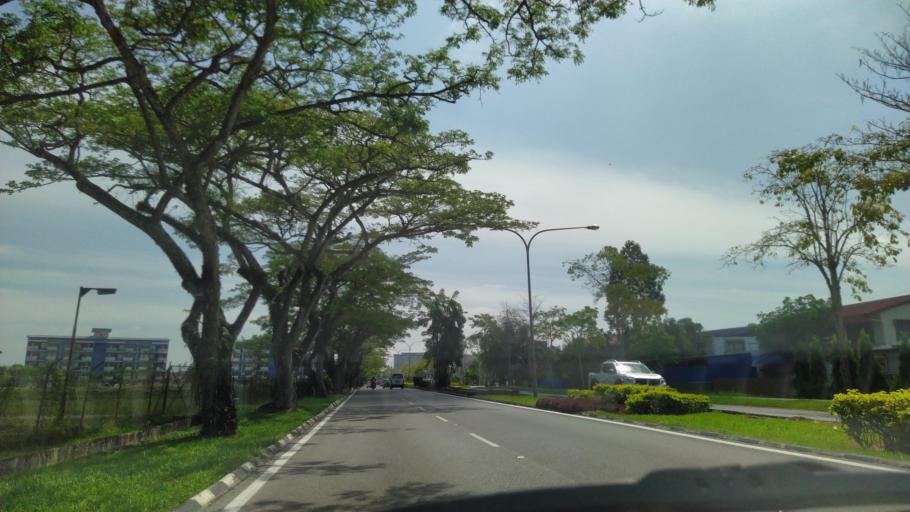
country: MY
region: Sarawak
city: Sibu
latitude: 2.3137
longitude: 111.8365
